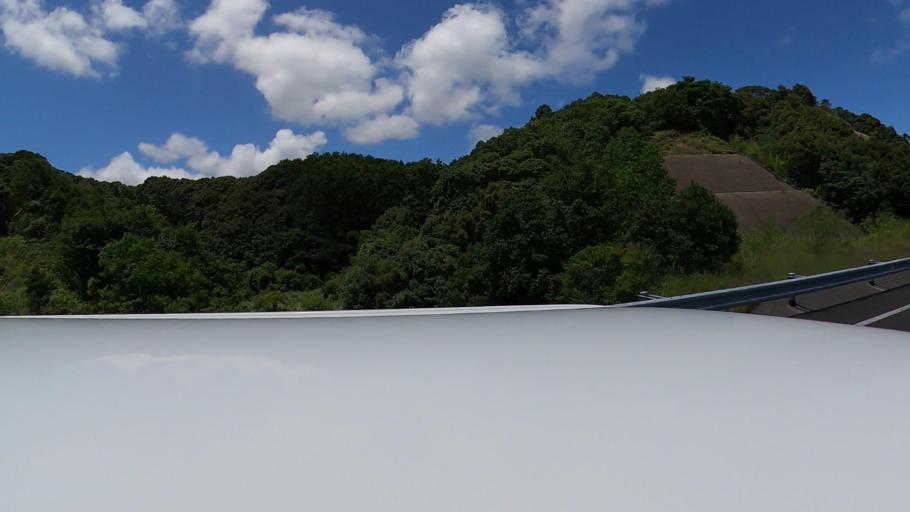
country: JP
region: Miyazaki
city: Nobeoka
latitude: 32.4963
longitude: 131.6592
